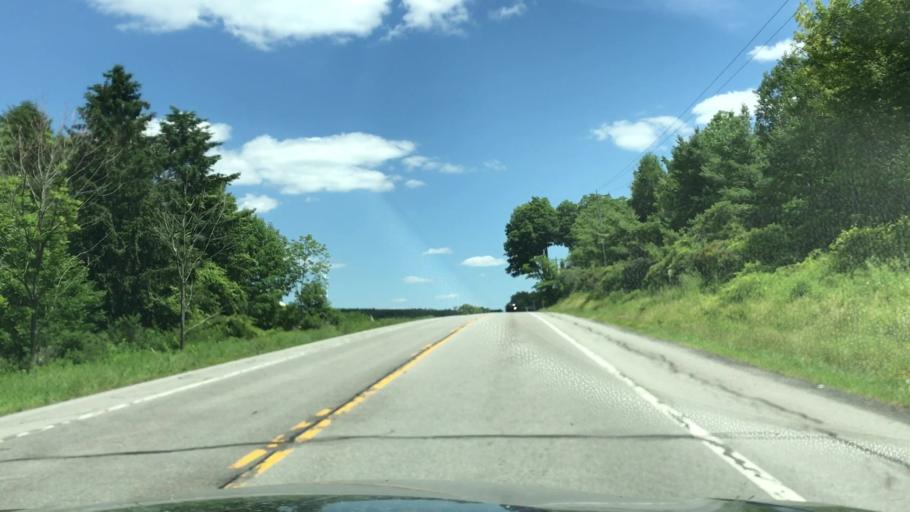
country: US
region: New York
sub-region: Wyoming County
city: Attica
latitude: 42.7515
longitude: -78.2550
